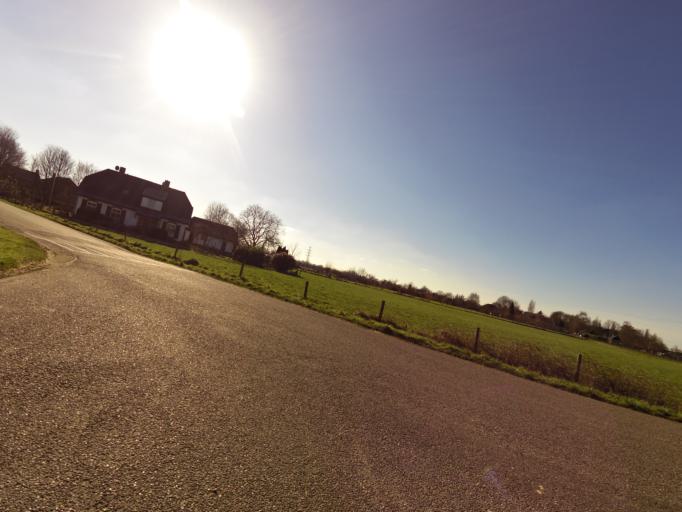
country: NL
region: Gelderland
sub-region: Gemeente Doesburg
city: Doesburg
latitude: 51.9404
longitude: 6.1582
